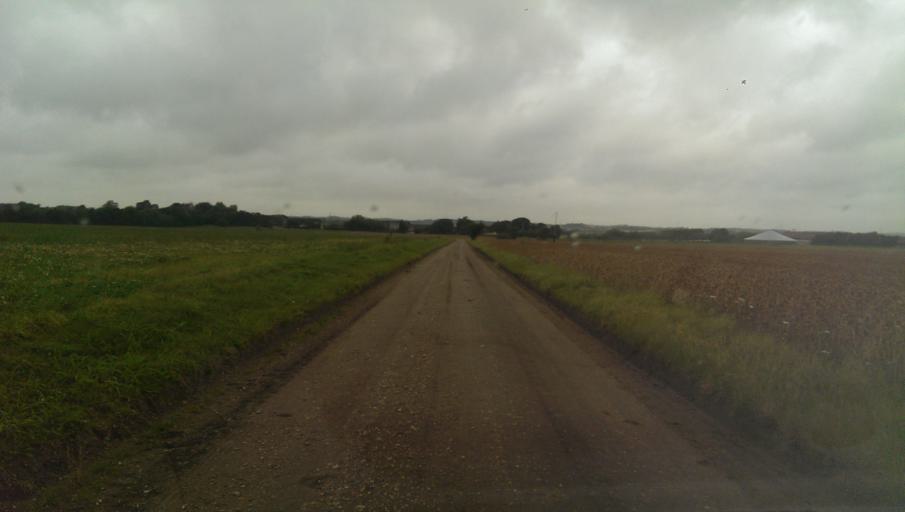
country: DK
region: South Denmark
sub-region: Esbjerg Kommune
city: Tjaereborg
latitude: 55.4865
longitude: 8.5984
